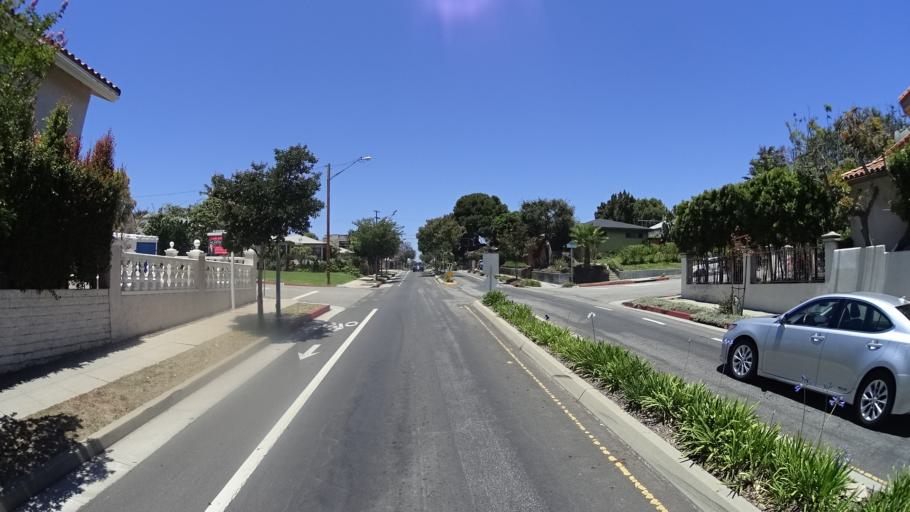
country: US
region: California
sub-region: Los Angeles County
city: Marina del Rey
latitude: 34.0119
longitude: -118.4592
